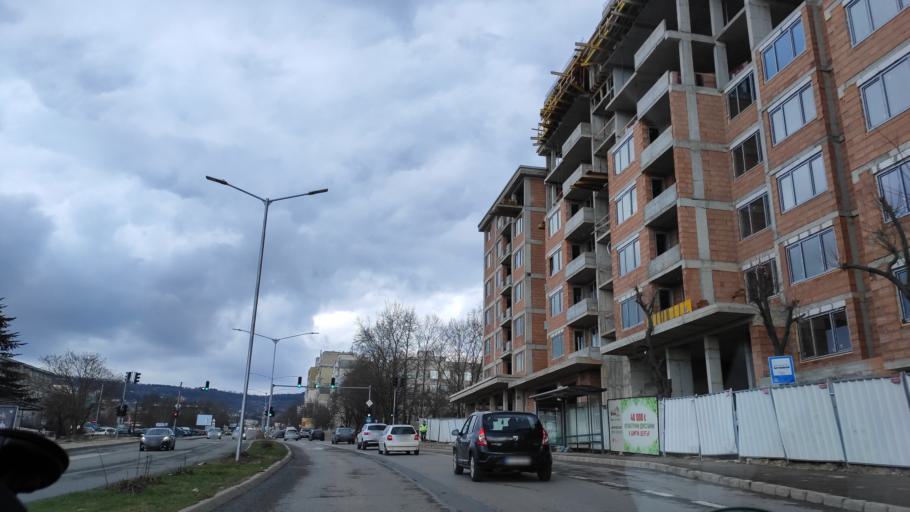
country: BG
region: Varna
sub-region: Obshtina Varna
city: Varna
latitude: 43.2296
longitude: 27.8793
